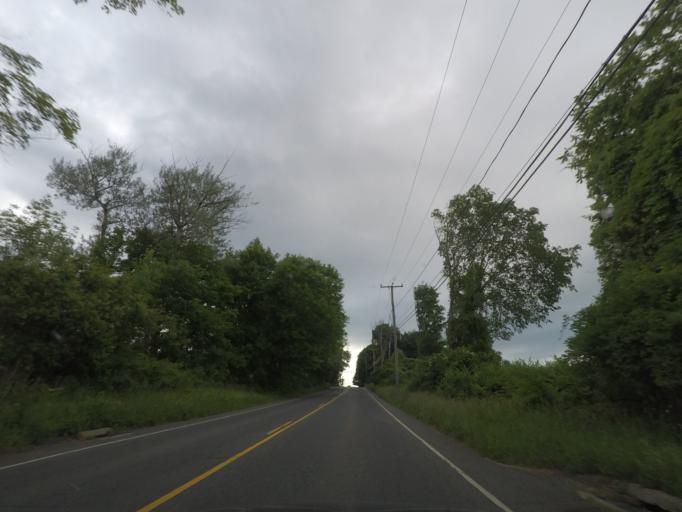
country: US
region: Connecticut
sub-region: Litchfield County
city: Canaan
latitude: 41.9320
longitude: -73.4231
